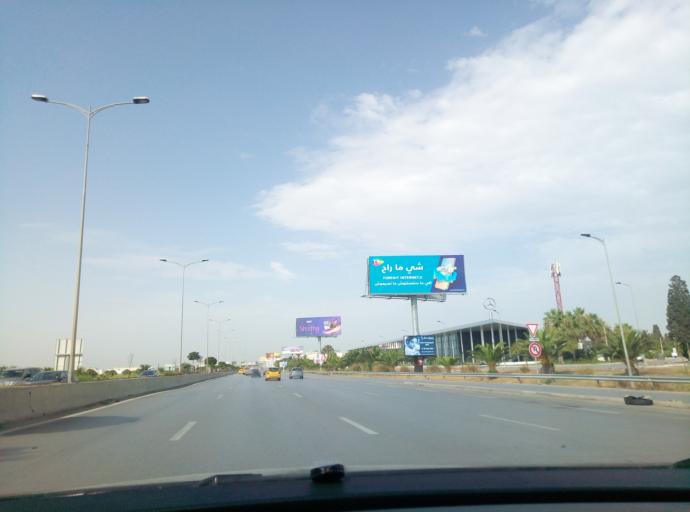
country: TN
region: Ariana
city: Ariana
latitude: 36.8307
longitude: 10.2104
